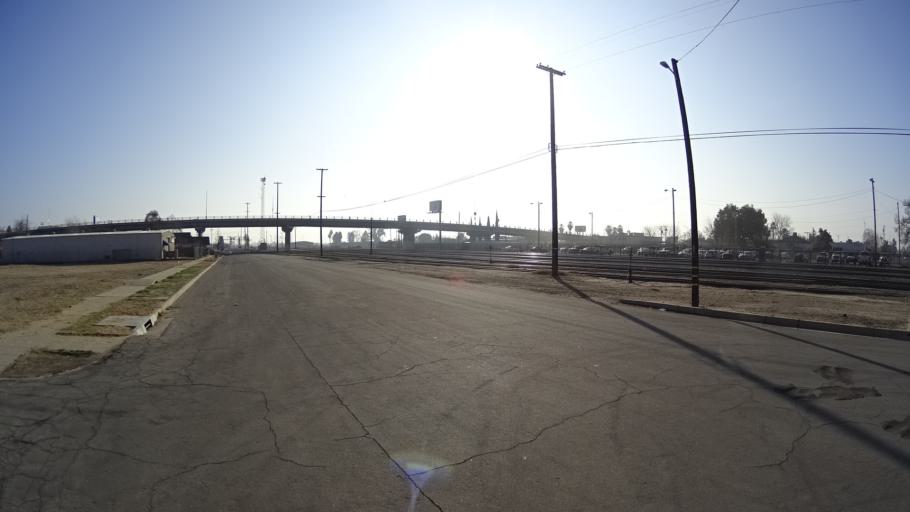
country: US
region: California
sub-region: Kern County
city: Bakersfield
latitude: 35.3775
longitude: -118.9911
